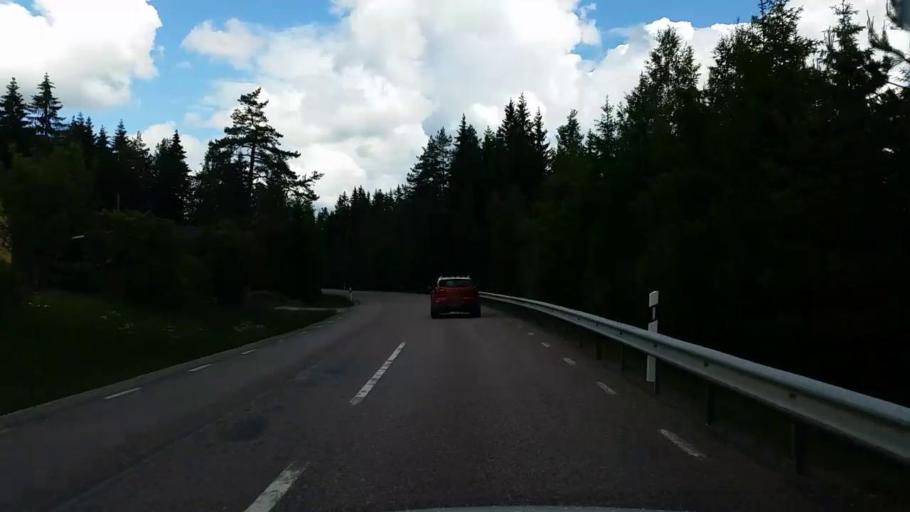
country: SE
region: Vaestmanland
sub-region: Fagersta Kommun
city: Fagersta
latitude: 59.8803
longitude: 15.8369
